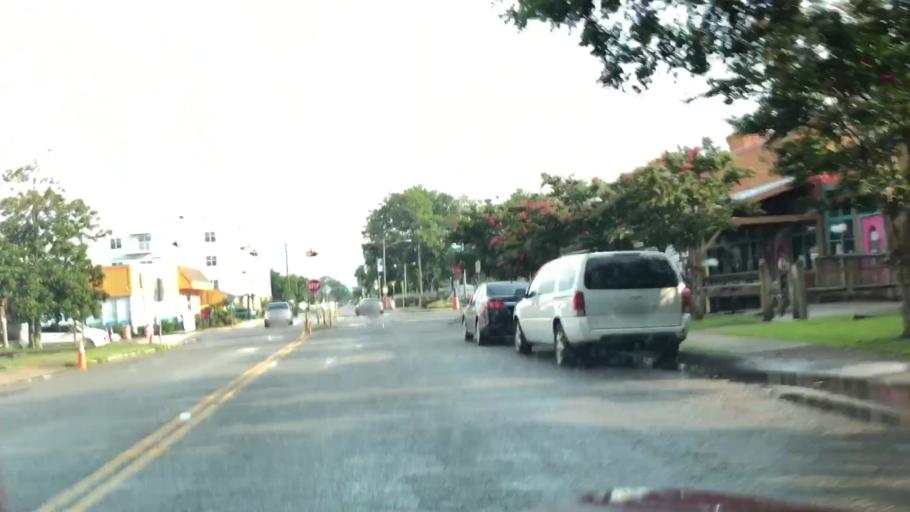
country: US
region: Virginia
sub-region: City of Virginia Beach
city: Virginia Beach
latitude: 36.8466
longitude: -75.9818
